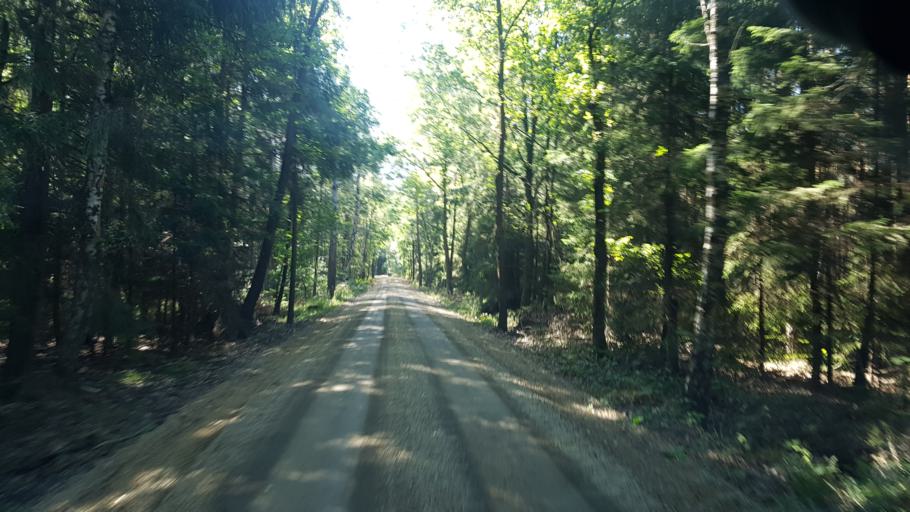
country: DE
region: Brandenburg
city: Hohenleipisch
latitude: 51.5325
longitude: 13.5828
